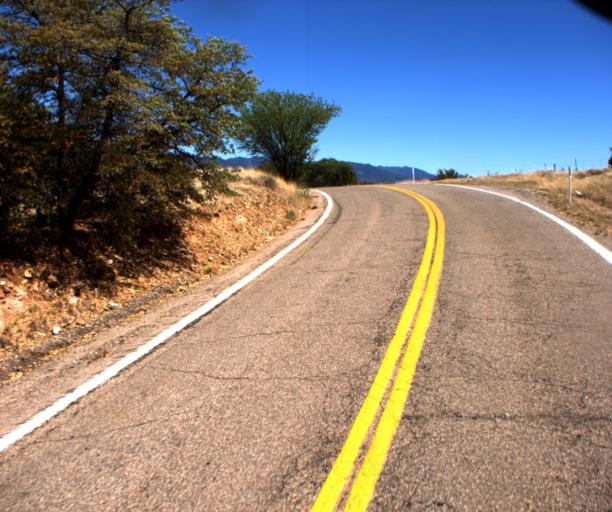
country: US
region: Arizona
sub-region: Cochise County
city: Huachuca City
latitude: 31.5520
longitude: -110.5476
